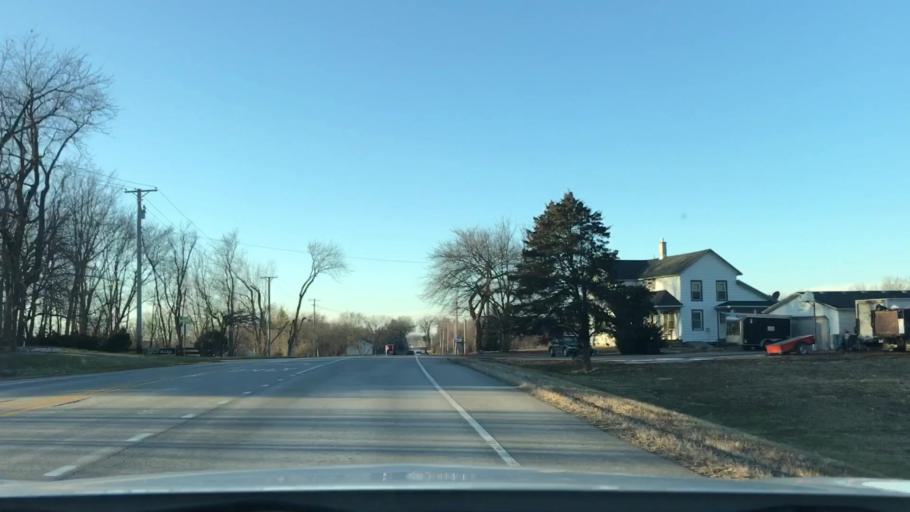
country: US
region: Illinois
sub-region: Kane County
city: Gilberts
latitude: 42.0796
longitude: -88.3805
